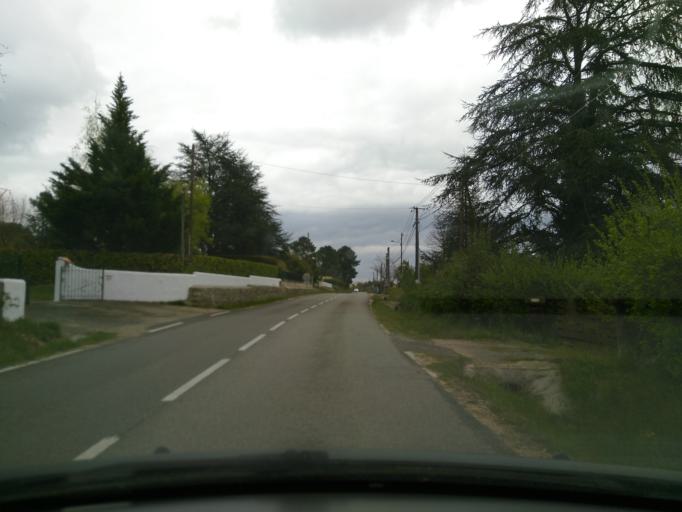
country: FR
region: Languedoc-Roussillon
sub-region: Departement du Gard
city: Barjac
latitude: 44.3788
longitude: 4.3715
